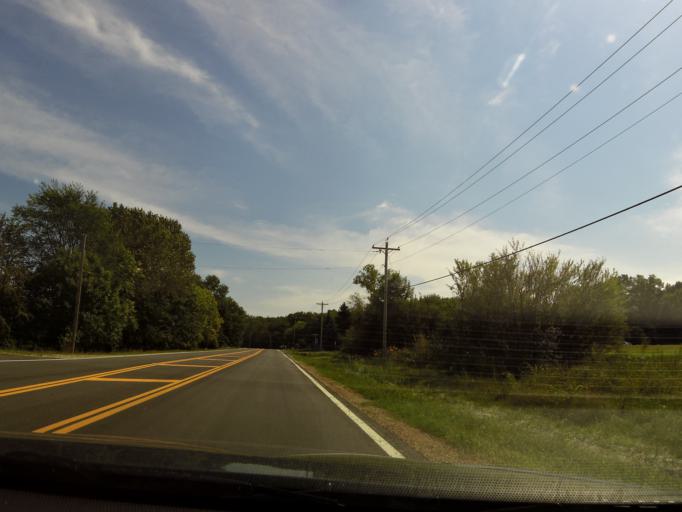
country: US
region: Minnesota
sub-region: Scott County
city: Prior Lake
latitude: 44.7643
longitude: -93.4133
